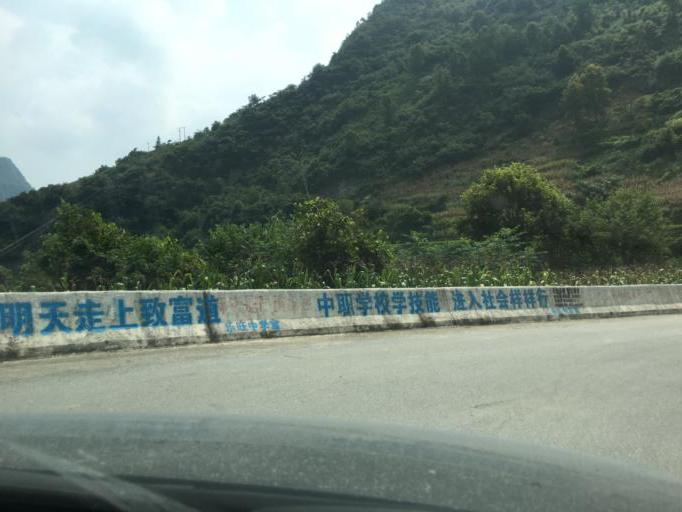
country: CN
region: Guangxi Zhuangzu Zizhiqu
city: Tongle
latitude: 25.2993
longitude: 106.2684
